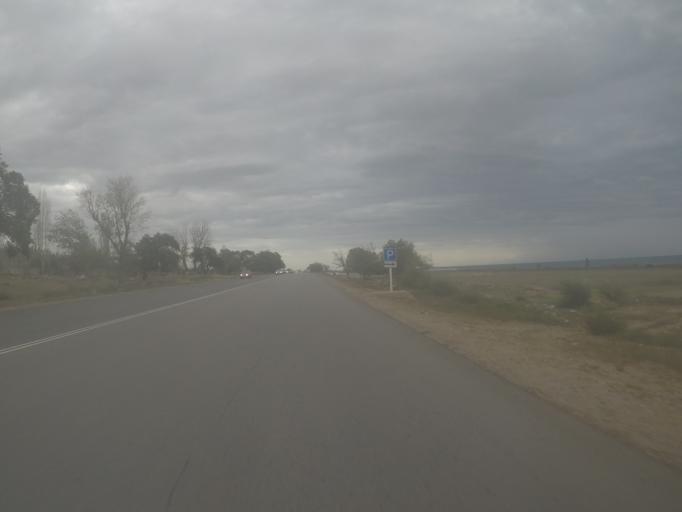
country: KG
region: Ysyk-Koel
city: Cholpon-Ata
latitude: 42.5970
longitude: 76.8358
